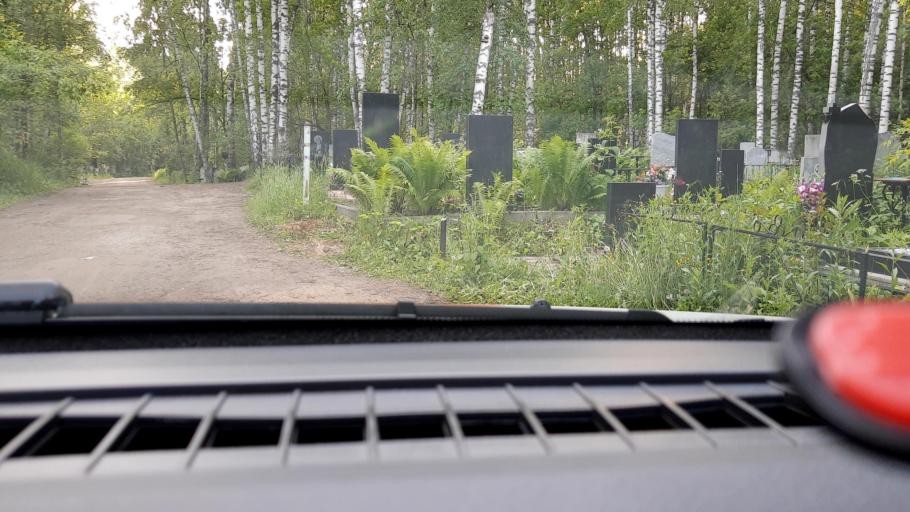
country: RU
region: Nizjnij Novgorod
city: Gorbatovka
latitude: 56.2325
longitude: 43.7761
